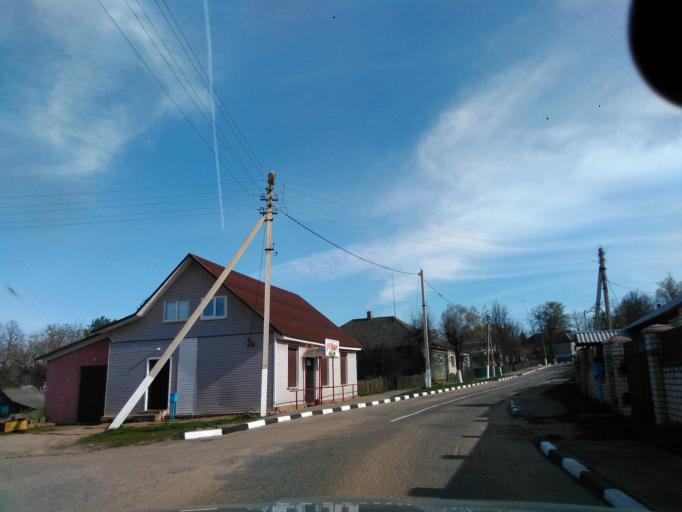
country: BY
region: Vitebsk
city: Chashniki
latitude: 54.8628
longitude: 29.1631
